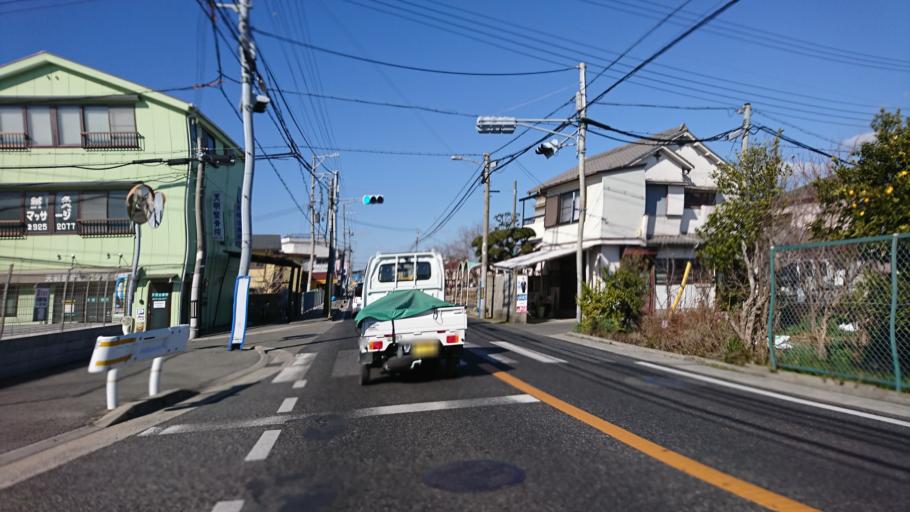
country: JP
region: Hyogo
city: Akashi
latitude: 34.6561
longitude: 134.9568
